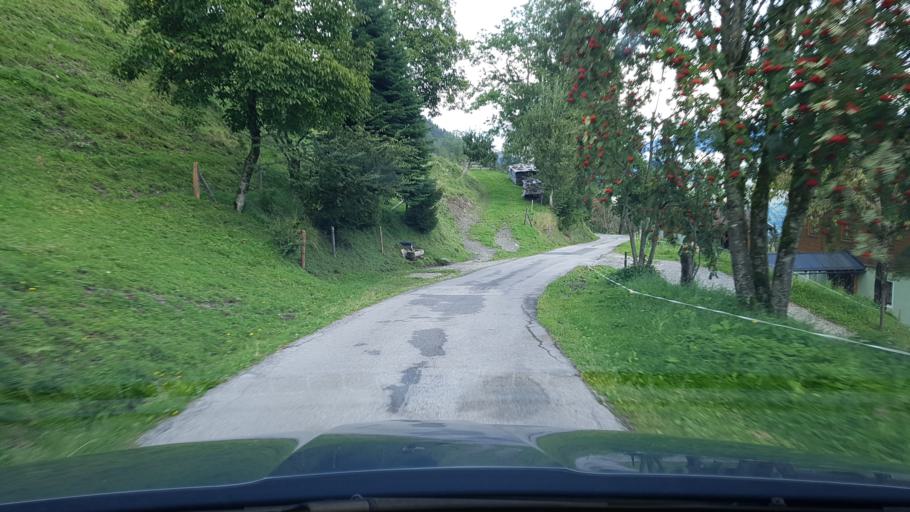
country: AT
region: Salzburg
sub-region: Politischer Bezirk Sankt Johann im Pongau
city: Goldegg
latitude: 47.3391
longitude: 13.0976
